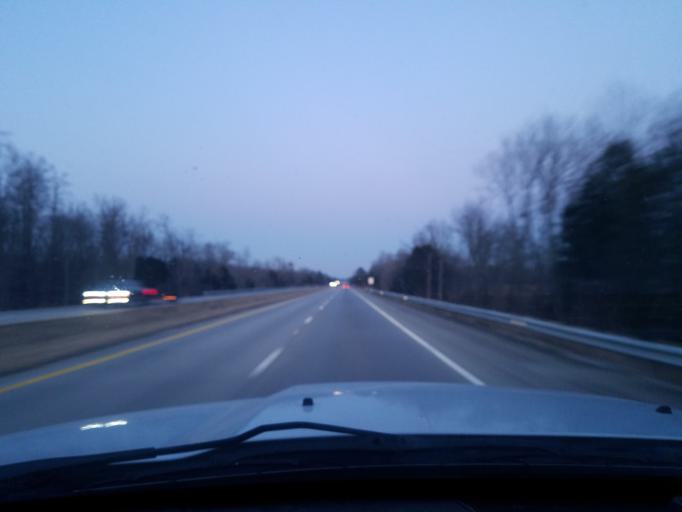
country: US
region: Kentucky
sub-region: Hardin County
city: Elizabethtown
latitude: 37.5848
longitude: -86.0093
